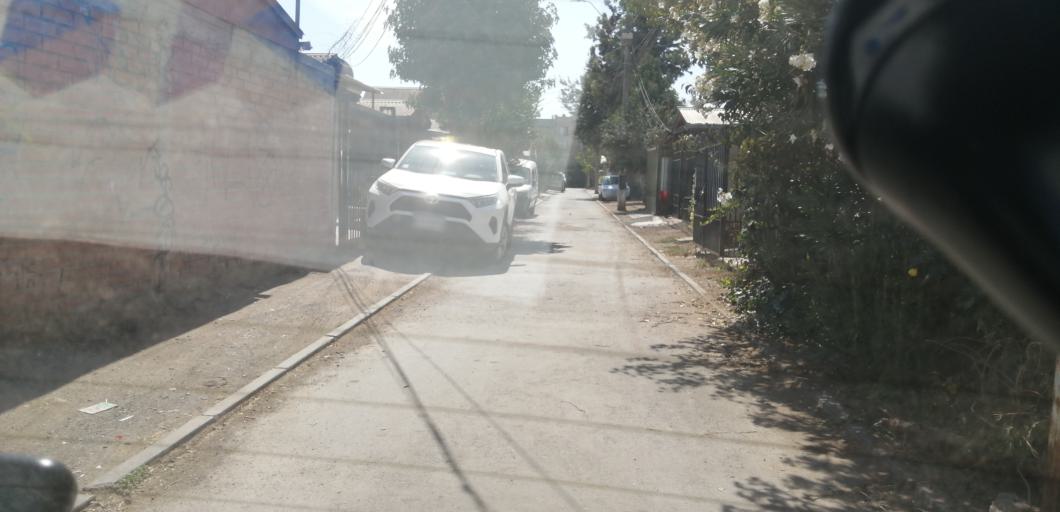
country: CL
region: Santiago Metropolitan
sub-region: Provincia de Santiago
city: Lo Prado
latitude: -33.4646
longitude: -70.7396
